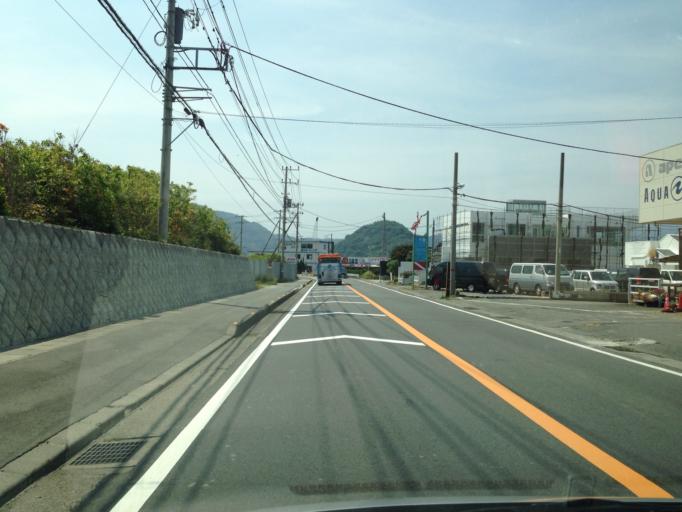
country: JP
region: Shizuoka
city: Numazu
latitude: 35.0487
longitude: 138.8864
